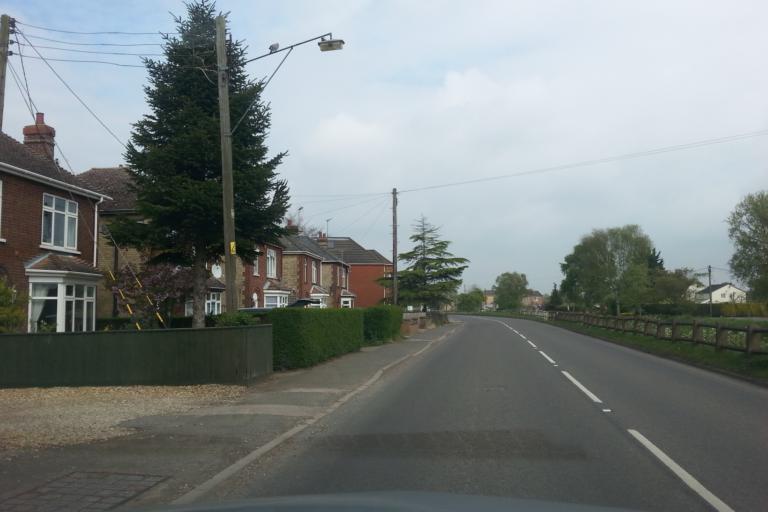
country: GB
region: England
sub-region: Norfolk
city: Outwell
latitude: 52.6058
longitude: 0.2277
